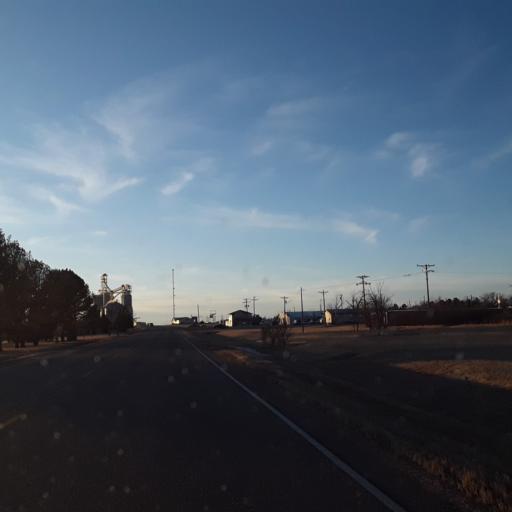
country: US
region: Colorado
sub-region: Cheyenne County
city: Cheyenne Wells
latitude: 38.8164
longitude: -102.3524
